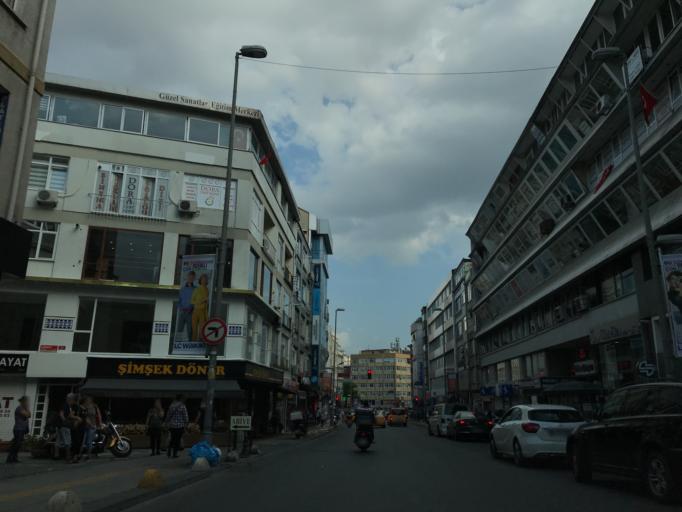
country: TR
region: Istanbul
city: UEskuedar
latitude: 40.9900
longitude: 29.0304
